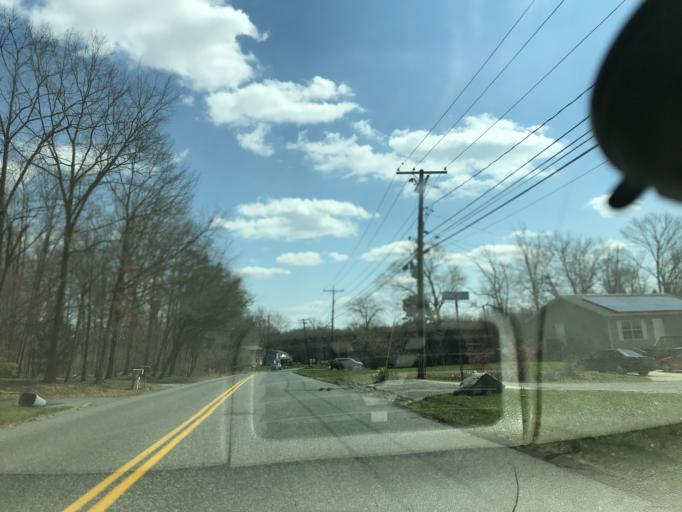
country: US
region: Maryland
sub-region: Harford County
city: Perryman
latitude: 39.4804
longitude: -76.2078
